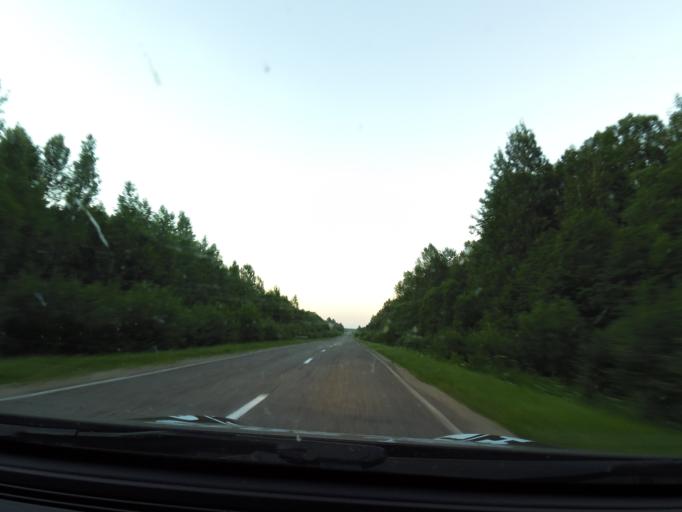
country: RU
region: Jaroslavl
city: Lyubim
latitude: 58.3326
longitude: 41.0678
